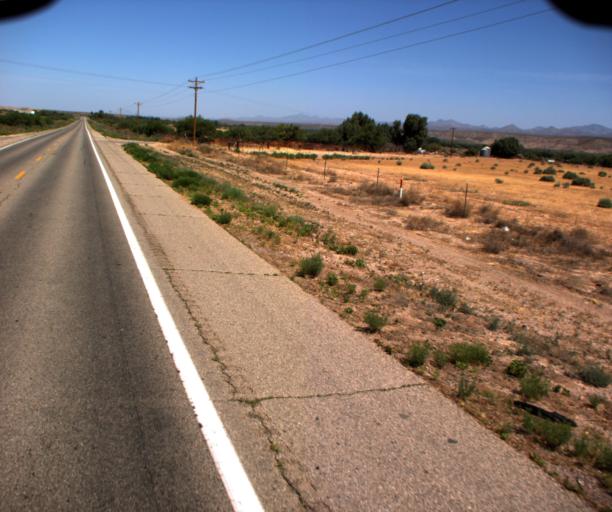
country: US
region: Arizona
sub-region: Graham County
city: Bylas
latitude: 33.0600
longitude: -110.0035
